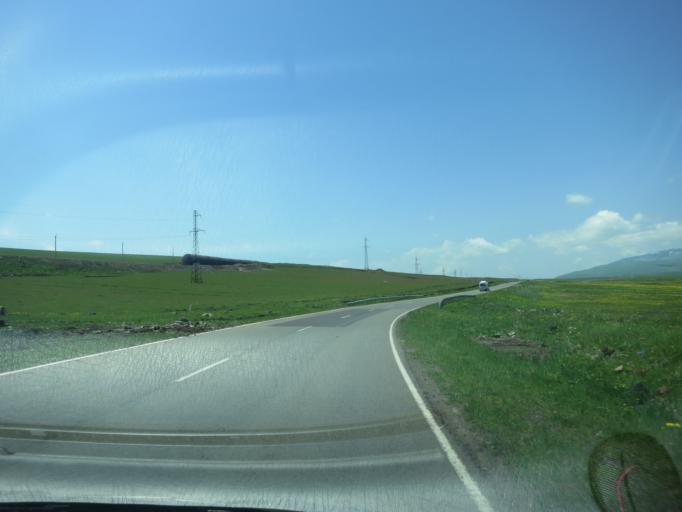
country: GE
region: Samtskhe-Javakheti
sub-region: Ninotsminda
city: Ninotsminda
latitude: 41.4128
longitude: 43.8308
